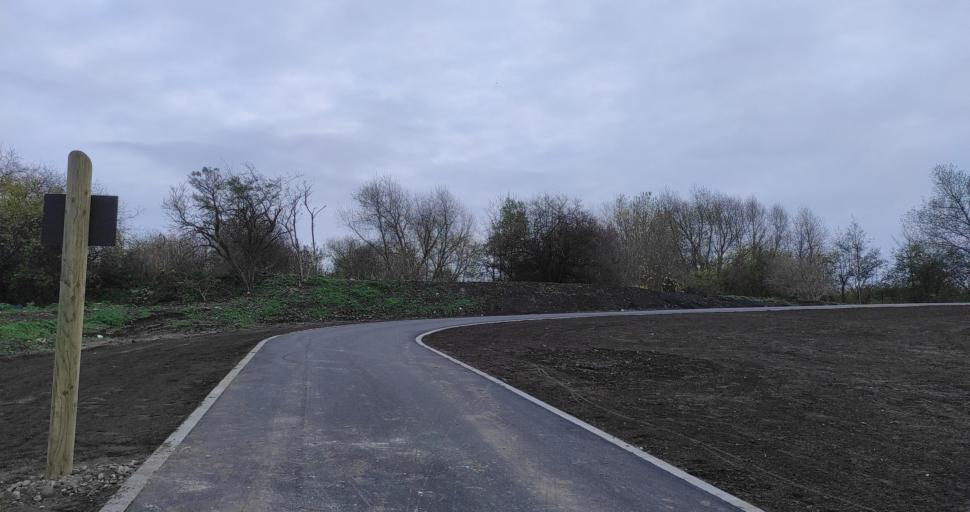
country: LV
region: Liepaja
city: Liepaja
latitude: 56.5172
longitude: 21.0378
